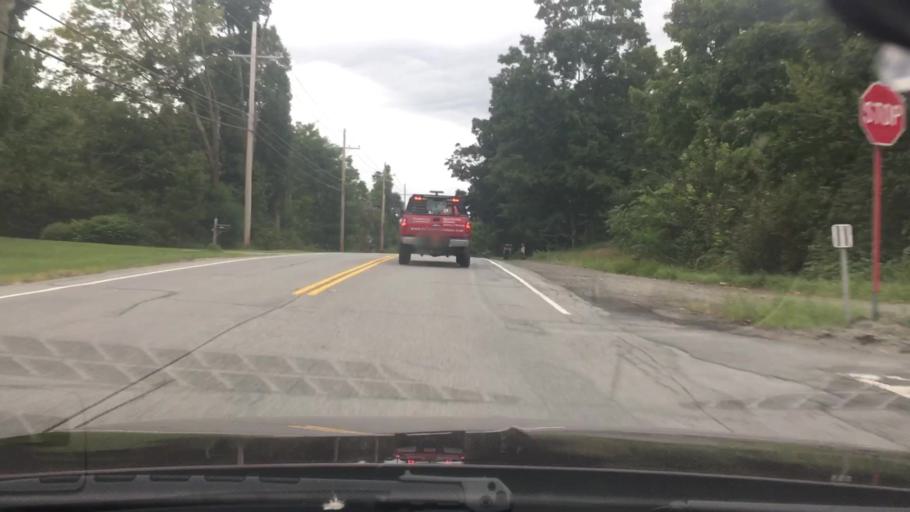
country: US
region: New York
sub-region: Dutchess County
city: Pleasant Valley
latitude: 41.7646
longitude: -73.7790
